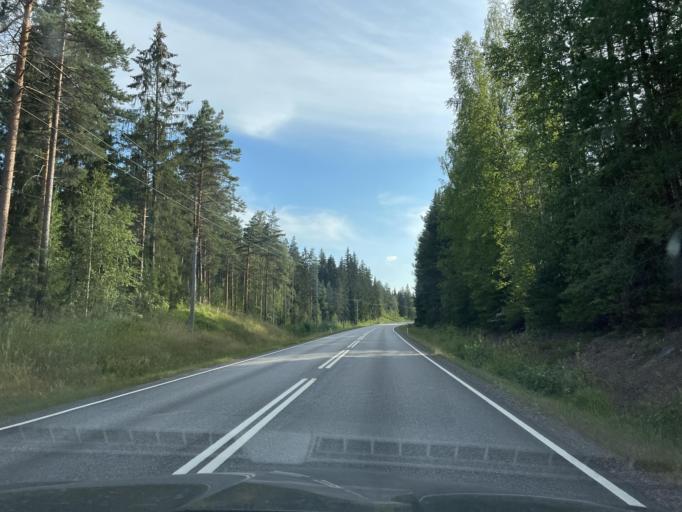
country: FI
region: Paijanne Tavastia
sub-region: Lahti
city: Padasjoki
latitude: 61.3336
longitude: 25.2178
